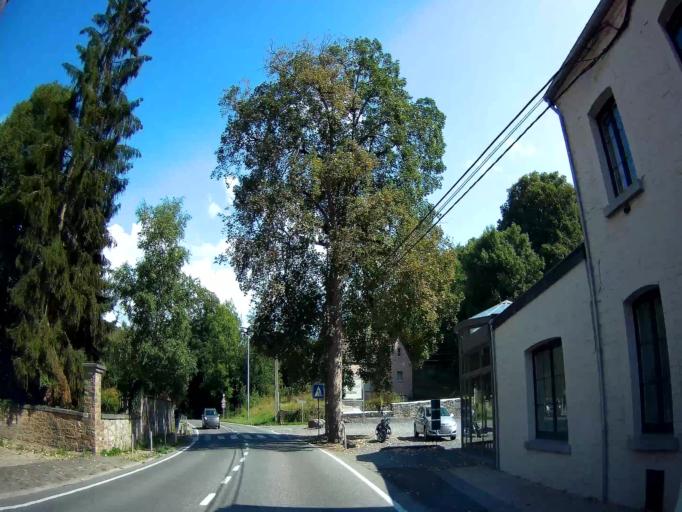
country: BE
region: Wallonia
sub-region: Province de Namur
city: Yvoir
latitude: 50.3364
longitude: 4.8665
